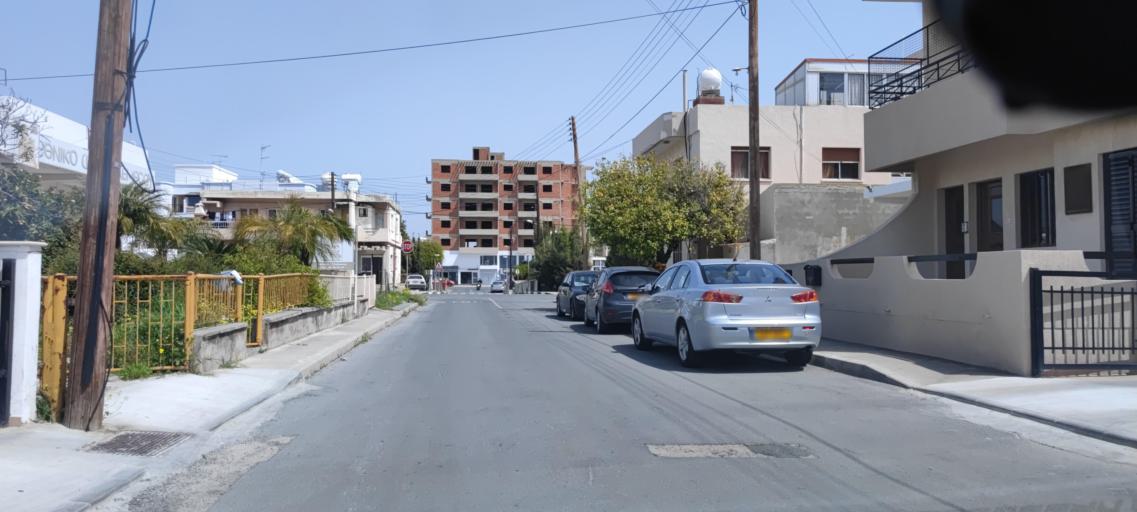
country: CY
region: Limassol
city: Limassol
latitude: 34.6835
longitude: 33.0227
